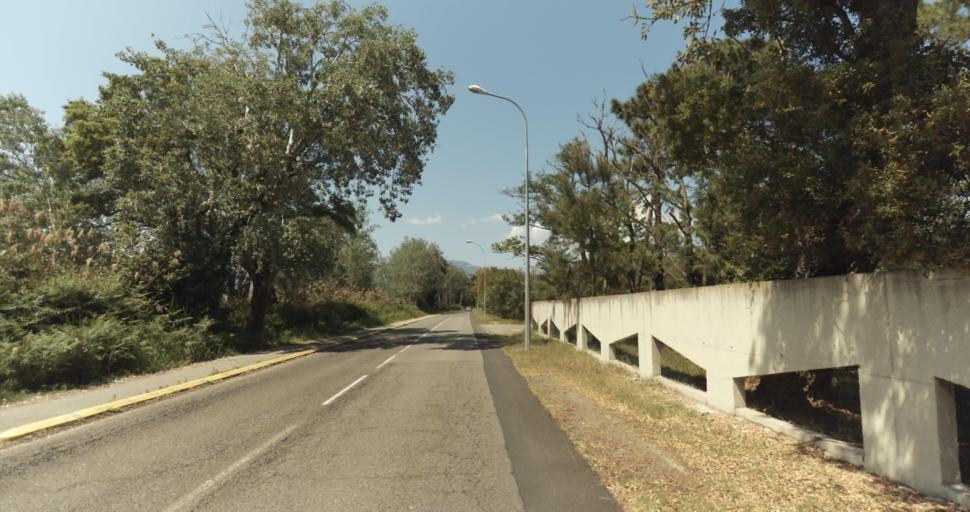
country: FR
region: Corsica
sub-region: Departement de la Haute-Corse
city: Biguglia
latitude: 42.6320
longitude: 9.4646
